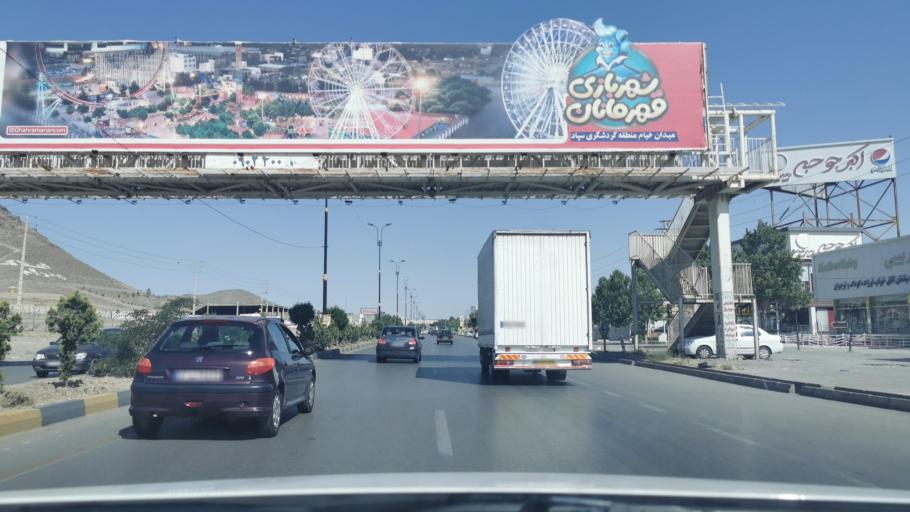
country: IR
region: Razavi Khorasan
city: Torqabeh
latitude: 36.3932
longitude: 59.4012
